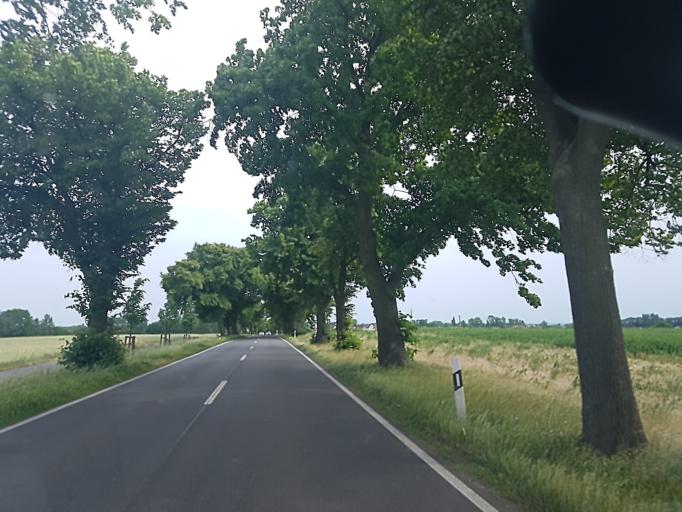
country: DE
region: Saxony-Anhalt
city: Wittenburg
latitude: 51.8854
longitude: 12.6268
